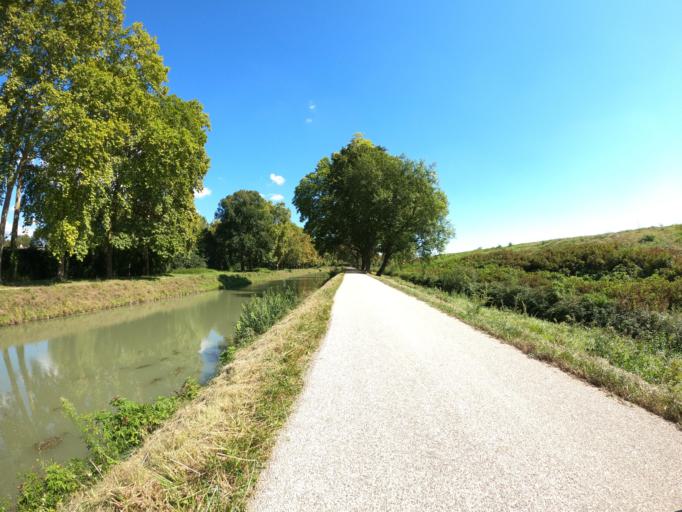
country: FR
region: Midi-Pyrenees
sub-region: Departement du Tarn-et-Garonne
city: Valence
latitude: 44.1042
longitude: 0.8945
